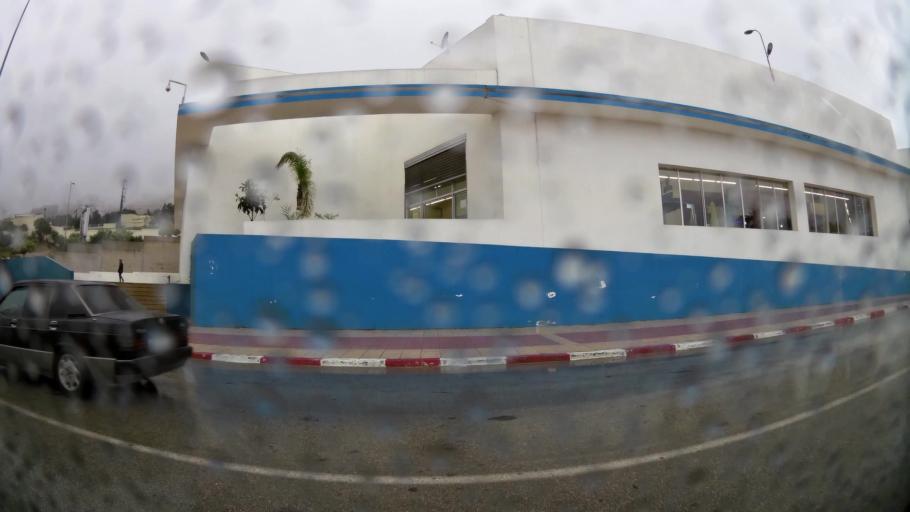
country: MA
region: Taza-Al Hoceima-Taounate
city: Al Hoceima
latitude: 35.2457
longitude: -3.9380
